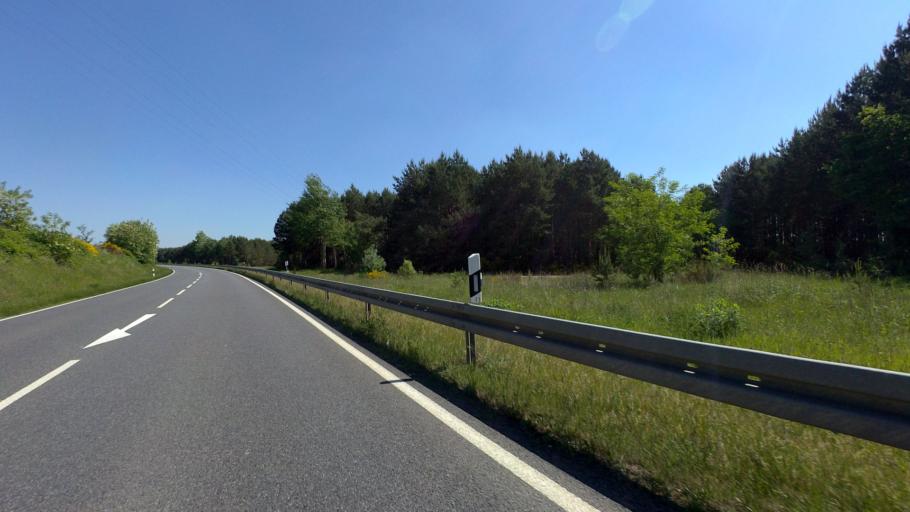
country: DE
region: Brandenburg
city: Spremberg
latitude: 51.5635
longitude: 14.3283
